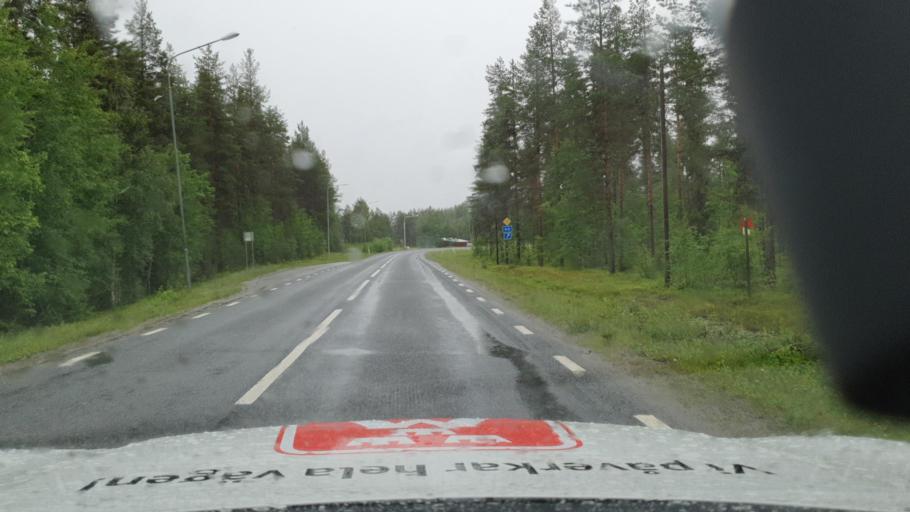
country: SE
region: Vaesterbotten
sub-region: Asele Kommun
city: Asele
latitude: 64.1564
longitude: 17.3854
